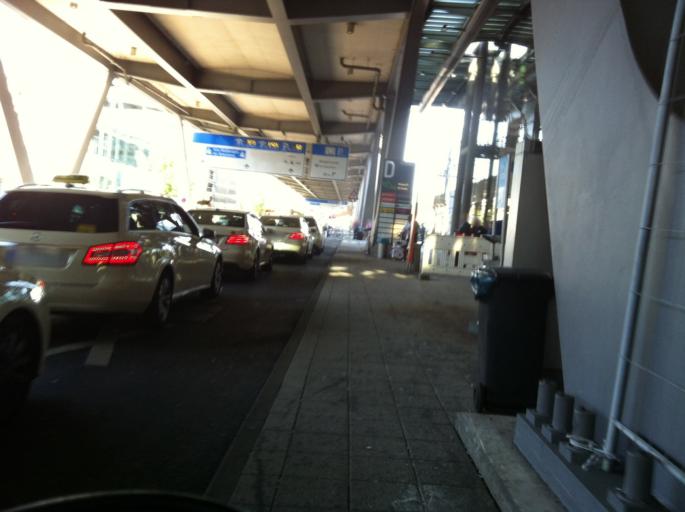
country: DE
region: North Rhine-Westphalia
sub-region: Regierungsbezirk Koln
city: Wahn-Heide
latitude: 50.8805
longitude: 7.1185
